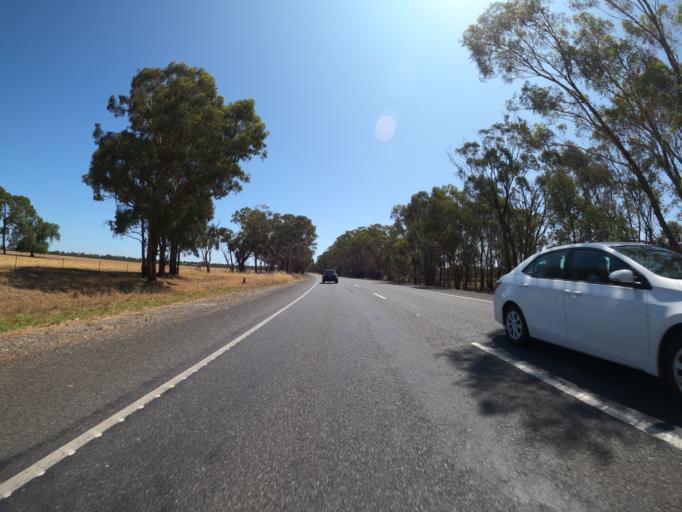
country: AU
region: New South Wales
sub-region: Corowa Shire
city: Corowa
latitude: -36.0588
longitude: 146.4278
